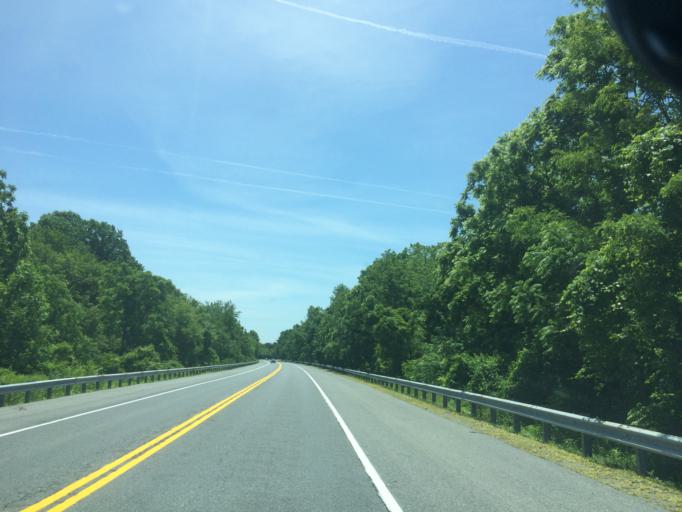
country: US
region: Maryland
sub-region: Carroll County
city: Eldersburg
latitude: 39.4523
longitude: -76.9994
